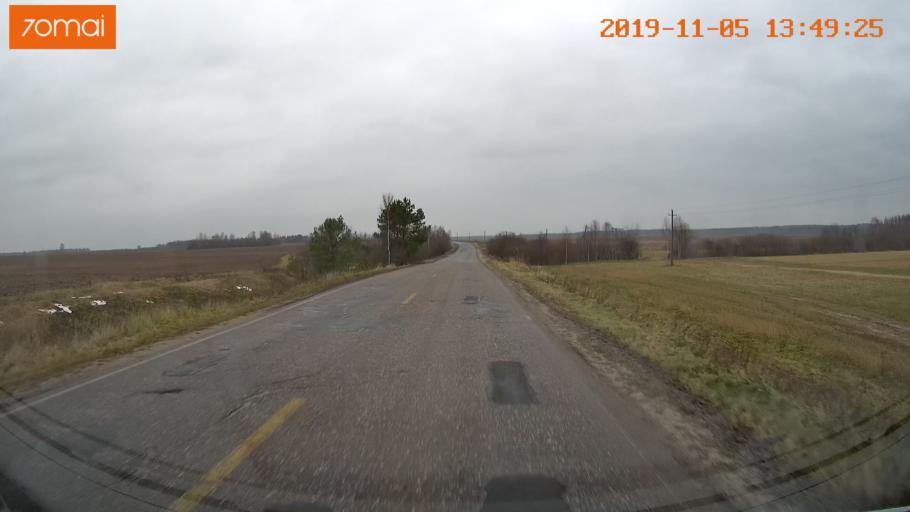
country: RU
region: Ivanovo
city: Kaminskiy
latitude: 57.0103
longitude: 41.4095
